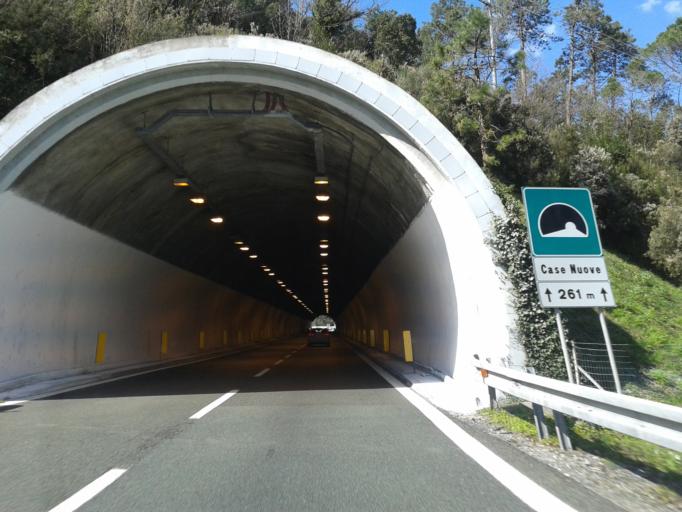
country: IT
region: Liguria
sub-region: Provincia di Genova
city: Casarza Ligure
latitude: 44.2691
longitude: 9.4540
